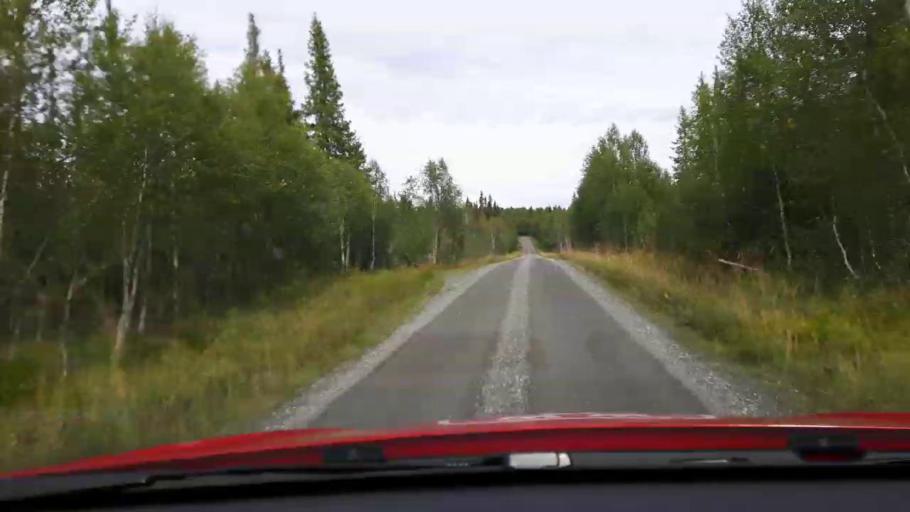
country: SE
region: Jaemtland
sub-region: Are Kommun
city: Are
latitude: 63.7810
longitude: 13.1010
